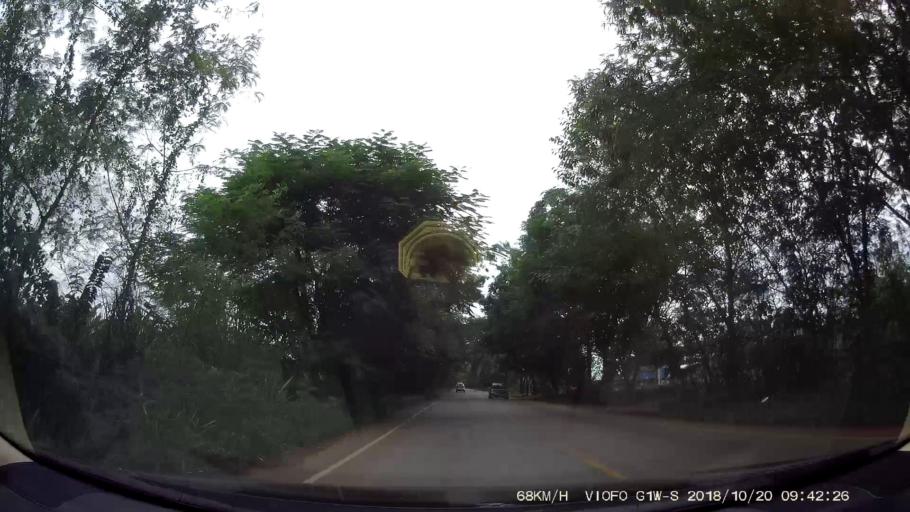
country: TH
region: Chaiyaphum
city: Khon San
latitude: 16.4636
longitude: 101.9524
